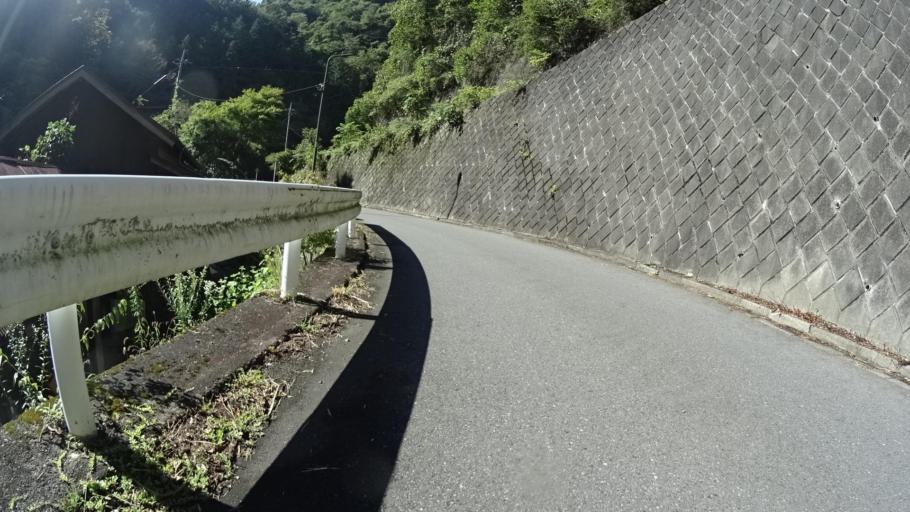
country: JP
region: Yamanashi
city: Uenohara
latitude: 35.7401
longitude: 139.0814
